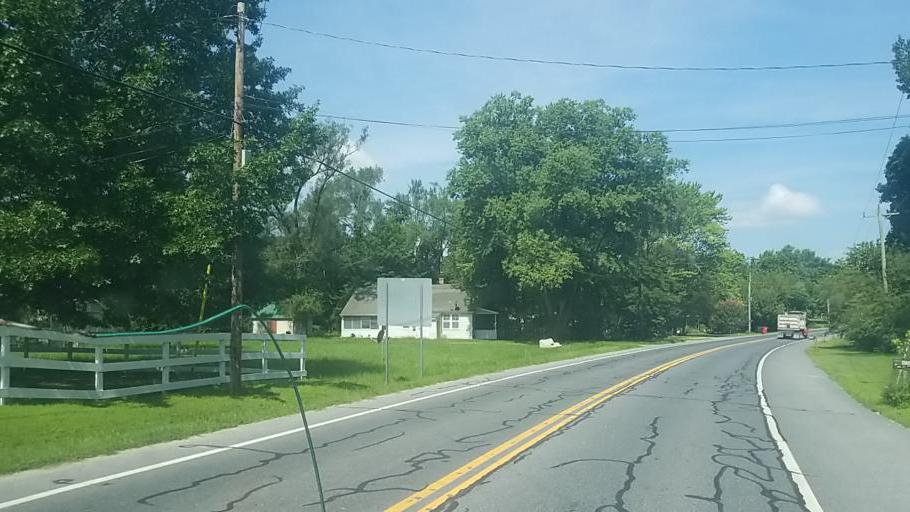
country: US
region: Delaware
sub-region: Sussex County
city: Seaford
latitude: 38.6683
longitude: -75.5706
